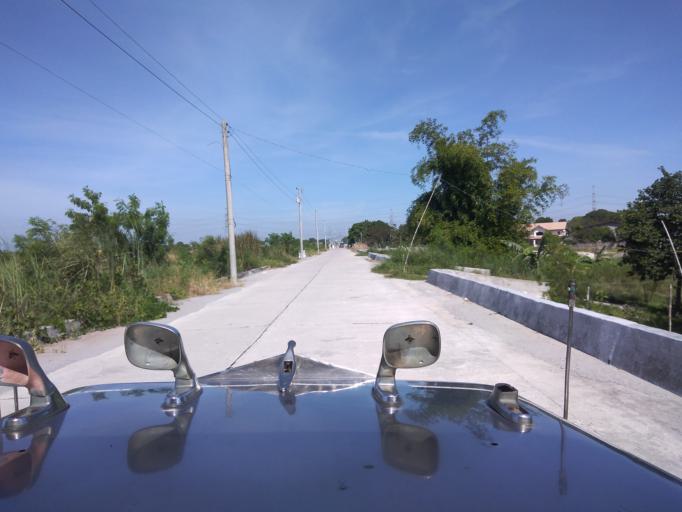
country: PH
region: Central Luzon
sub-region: Province of Pampanga
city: Bacolor
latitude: 15.0040
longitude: 120.6601
